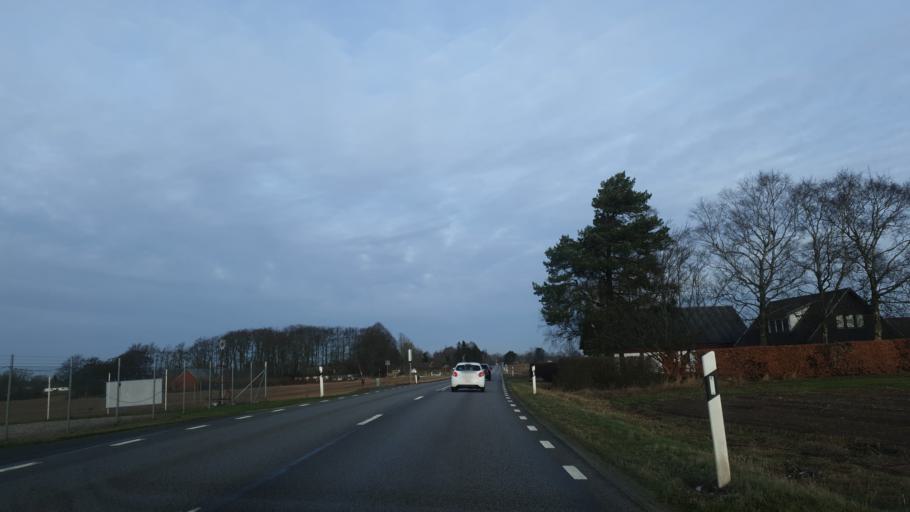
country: SE
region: Skane
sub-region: Horby Kommun
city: Hoerby
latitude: 55.7777
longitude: 13.6745
